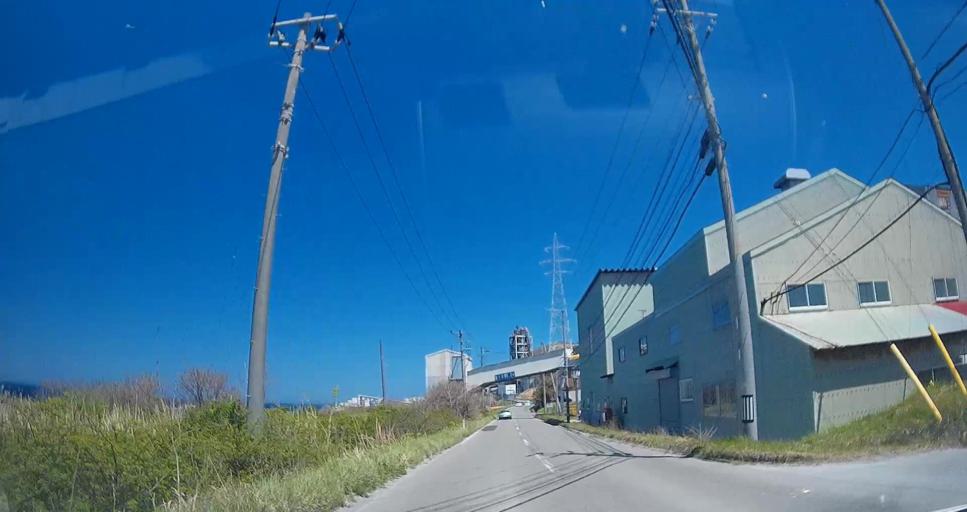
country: JP
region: Aomori
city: Mutsu
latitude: 41.4033
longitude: 141.4300
